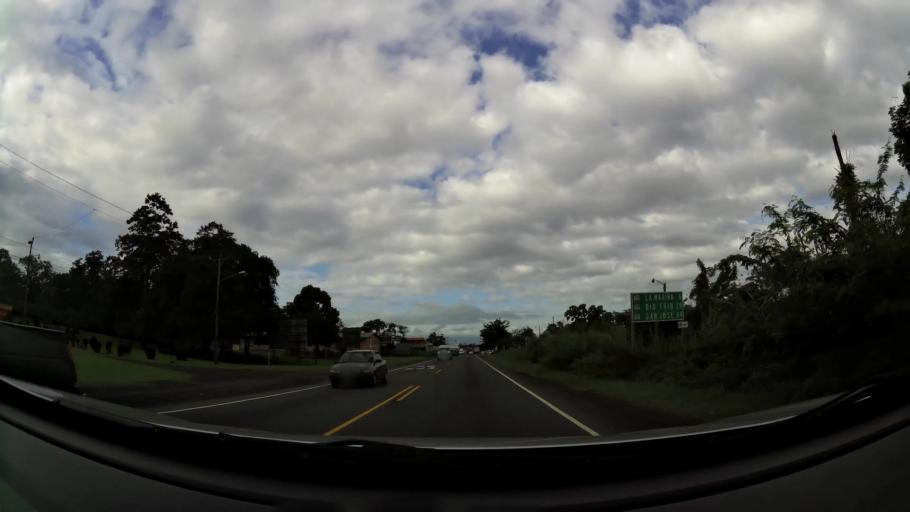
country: CR
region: Limon
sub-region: Canton de Pococi
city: Guapiles
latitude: 10.2023
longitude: -83.7922
